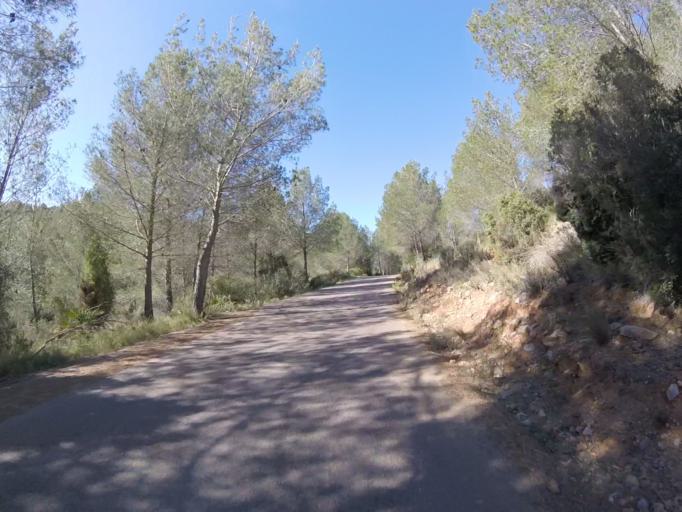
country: ES
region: Valencia
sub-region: Provincia de Castello
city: Benicassim
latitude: 40.0780
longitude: 0.0976
